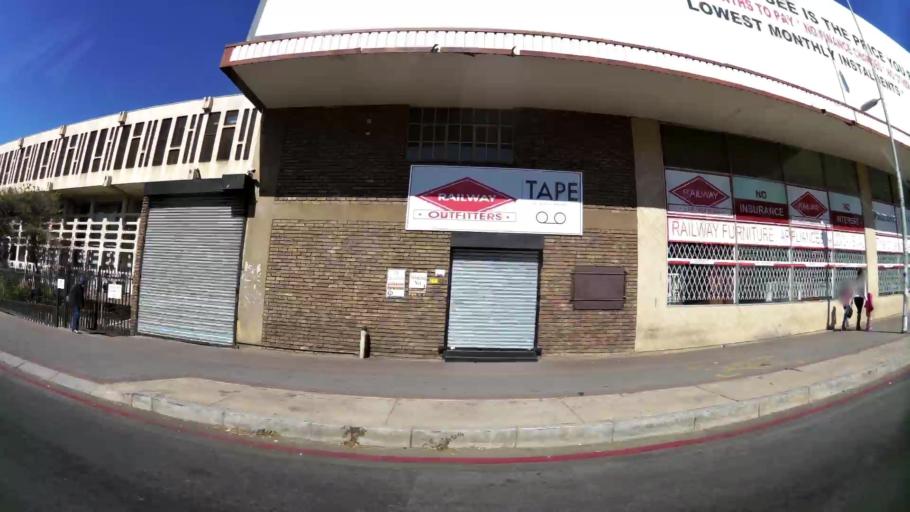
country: ZA
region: Gauteng
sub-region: City of Tshwane Metropolitan Municipality
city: Pretoria
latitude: -25.7507
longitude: 28.1886
